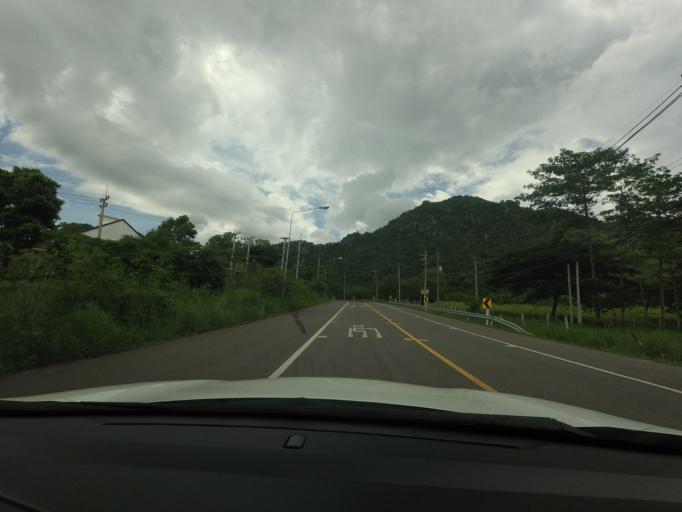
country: TH
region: Sara Buri
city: Muak Lek
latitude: 14.5493
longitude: 101.3258
